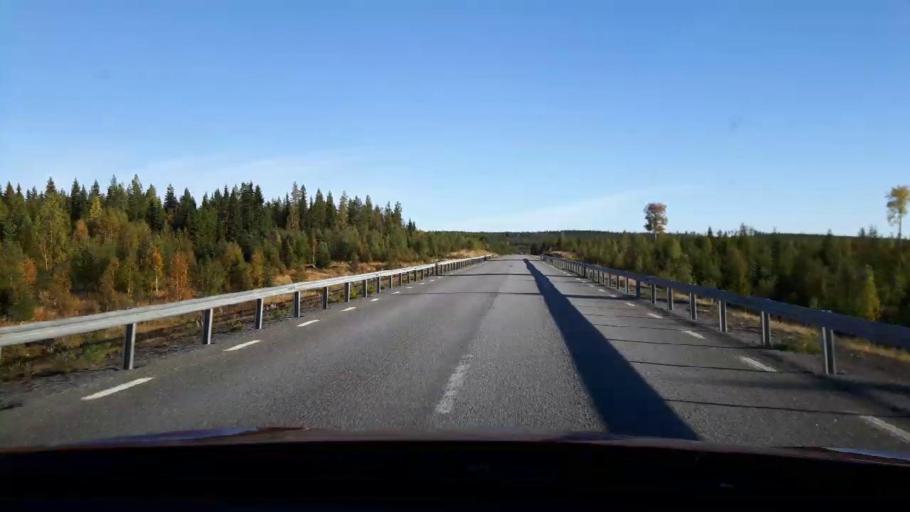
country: SE
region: Jaemtland
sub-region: OEstersunds Kommun
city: Lit
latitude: 63.7737
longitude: 14.7143
